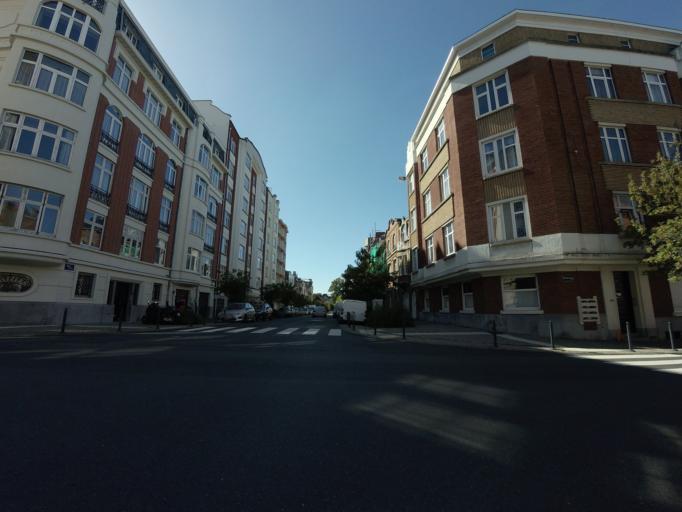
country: BE
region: Brussels Capital
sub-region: Bruxelles-Capitale
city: Brussels
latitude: 50.8489
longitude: 4.3972
